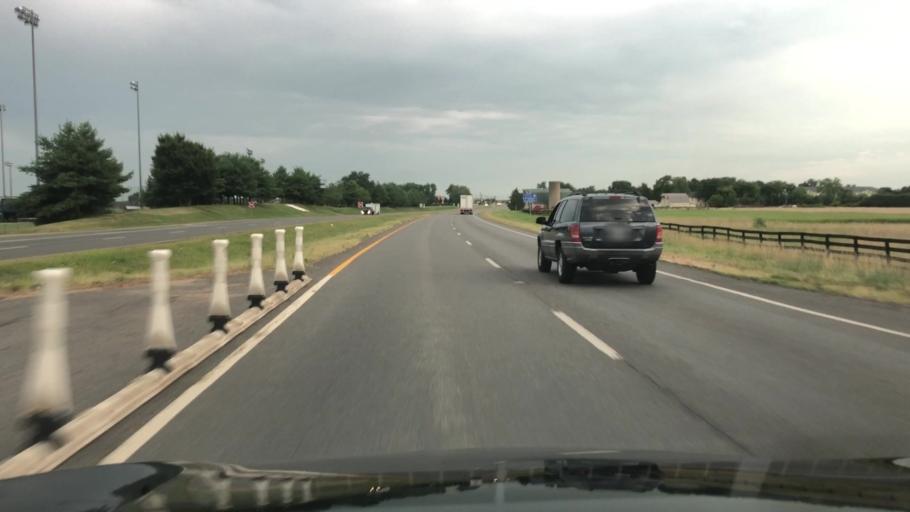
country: US
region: Virginia
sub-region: Fauquier County
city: Bealeton
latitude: 38.5895
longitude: -77.7699
